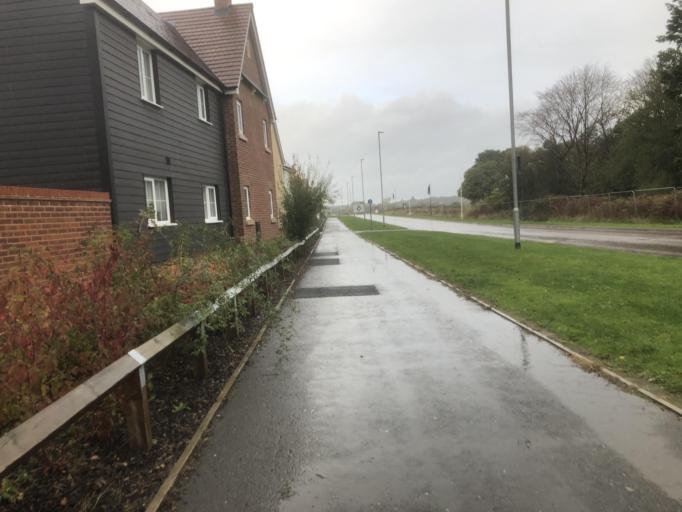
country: GB
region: England
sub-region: Norfolk
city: Spixworth
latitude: 52.6563
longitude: 1.3496
